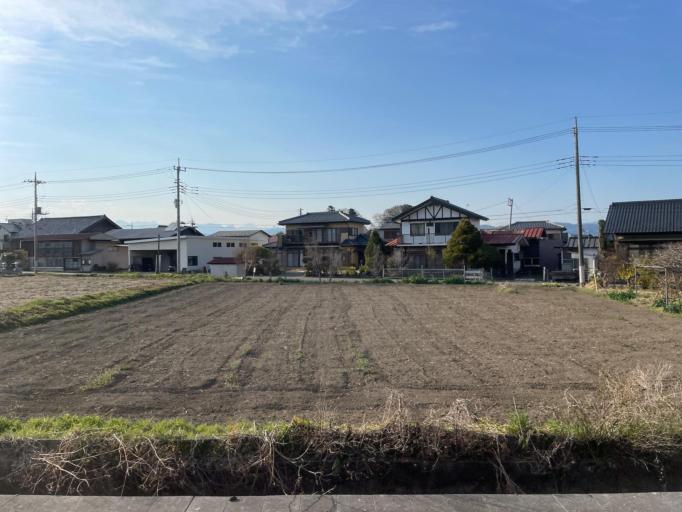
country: JP
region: Gunma
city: Annaka
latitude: 36.3072
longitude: 138.8750
